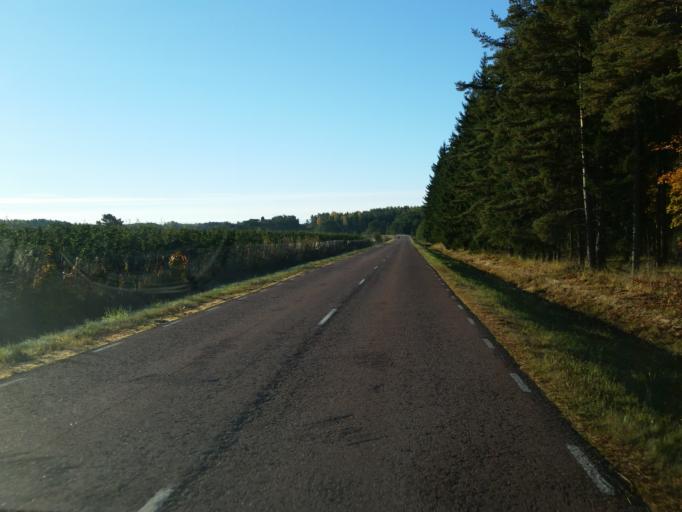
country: AX
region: Alands skaergard
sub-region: Vardoe
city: Vardoe
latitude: 60.2411
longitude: 20.3735
